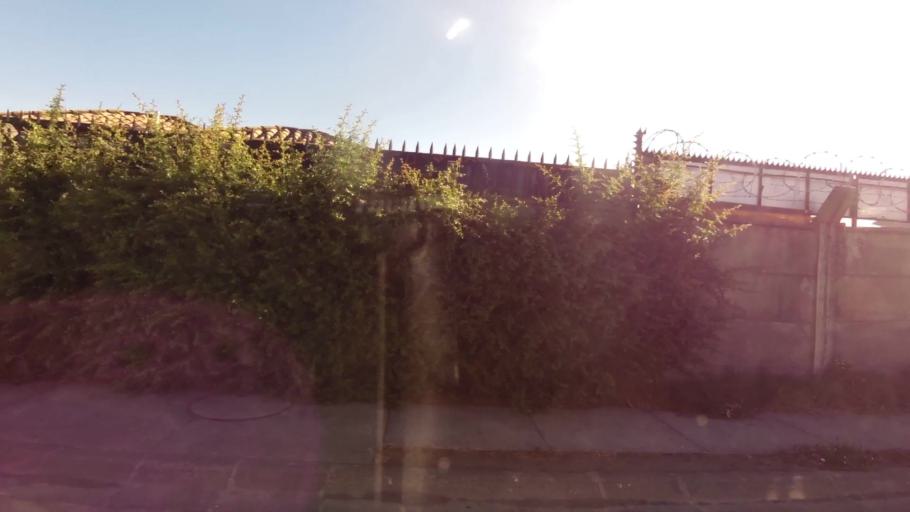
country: CL
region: O'Higgins
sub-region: Provincia de Cachapoal
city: Rancagua
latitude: -34.1935
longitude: -70.7199
